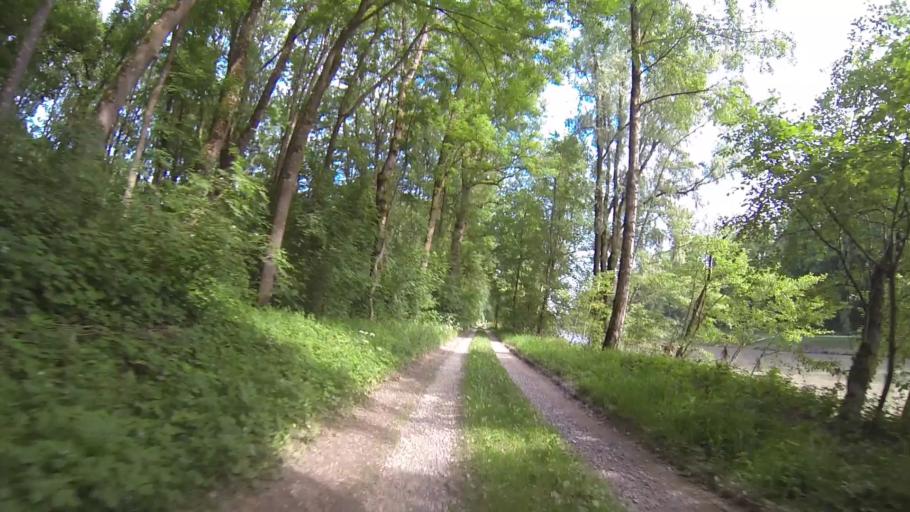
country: DE
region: Bavaria
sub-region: Swabia
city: Senden
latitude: 48.3446
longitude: 10.0074
